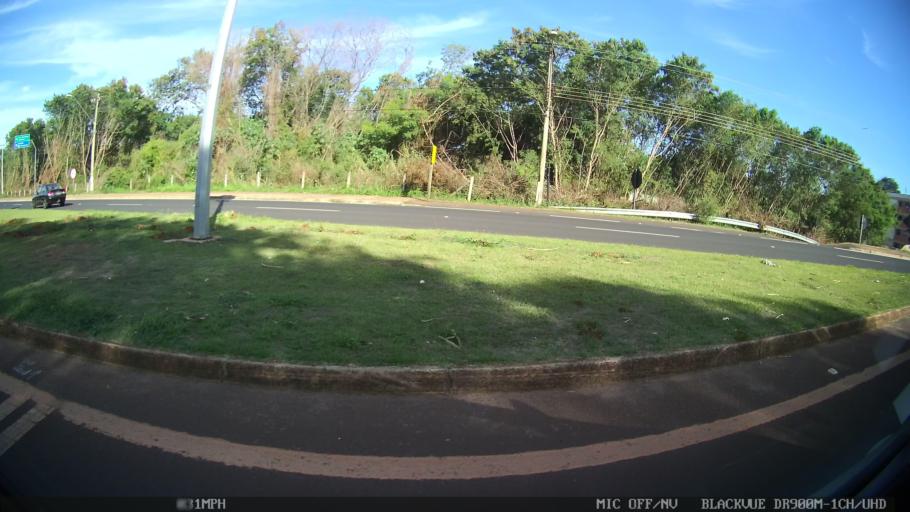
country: BR
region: Sao Paulo
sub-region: Araraquara
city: Araraquara
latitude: -21.7905
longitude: -48.1453
